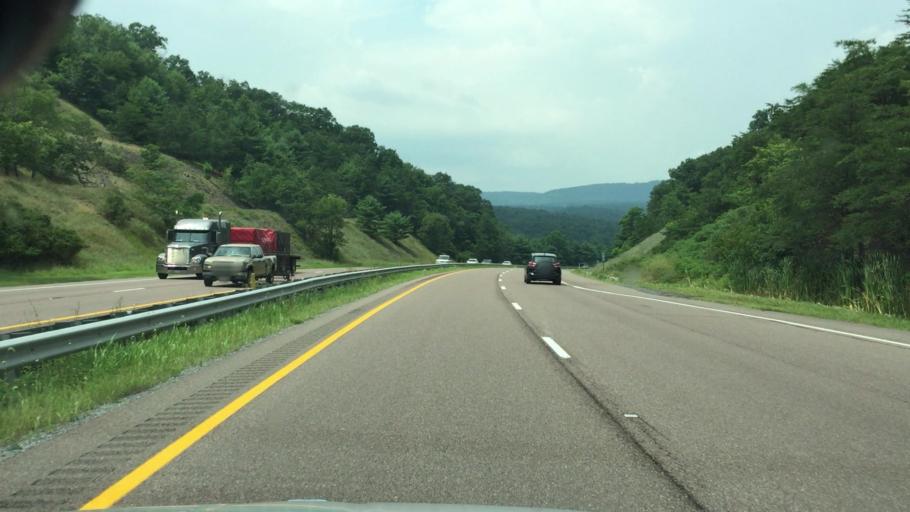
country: US
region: West Virginia
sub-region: Morgan County
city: Berkeley Springs
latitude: 39.6684
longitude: -78.4505
